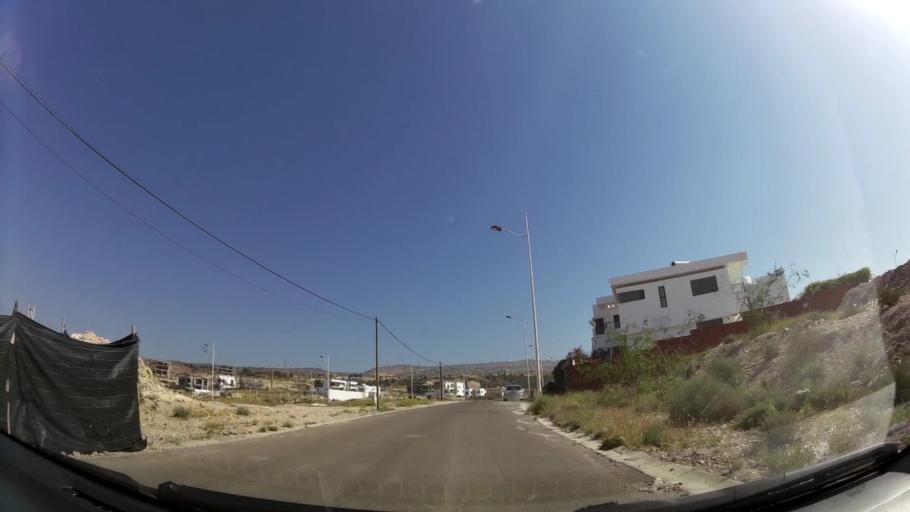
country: MA
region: Souss-Massa-Draa
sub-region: Agadir-Ida-ou-Tnan
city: Agadir
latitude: 30.4405
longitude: -9.5760
